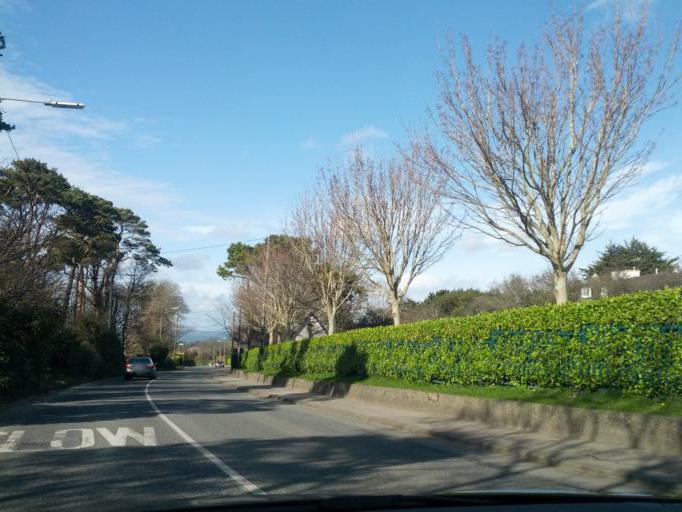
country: IE
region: Leinster
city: Sutton
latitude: 53.3739
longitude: -6.0898
